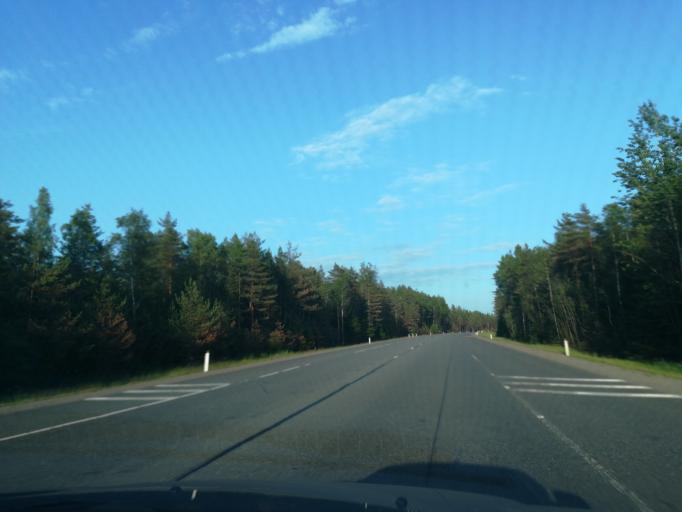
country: RU
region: Leningrad
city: Veshchevo
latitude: 60.6323
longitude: 29.0365
